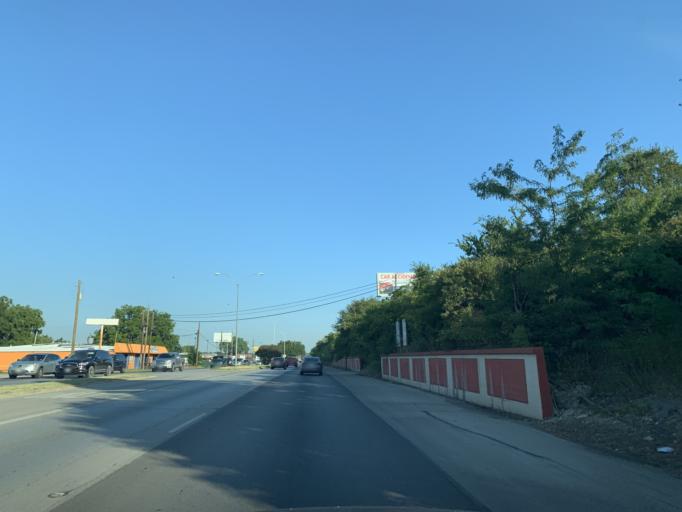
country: US
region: Texas
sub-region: Tarrant County
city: River Oaks
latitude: 32.7695
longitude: -97.3579
